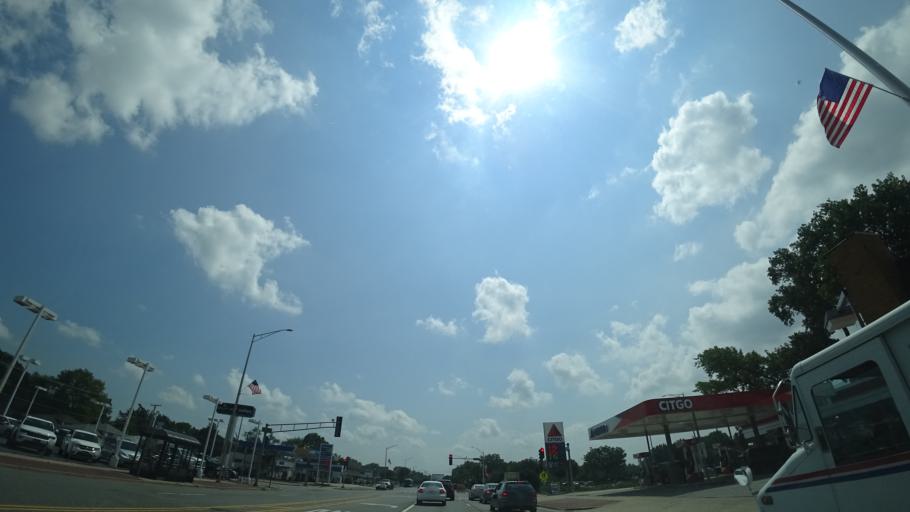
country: US
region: Illinois
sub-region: Cook County
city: Worth
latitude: 41.6832
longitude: -87.7972
